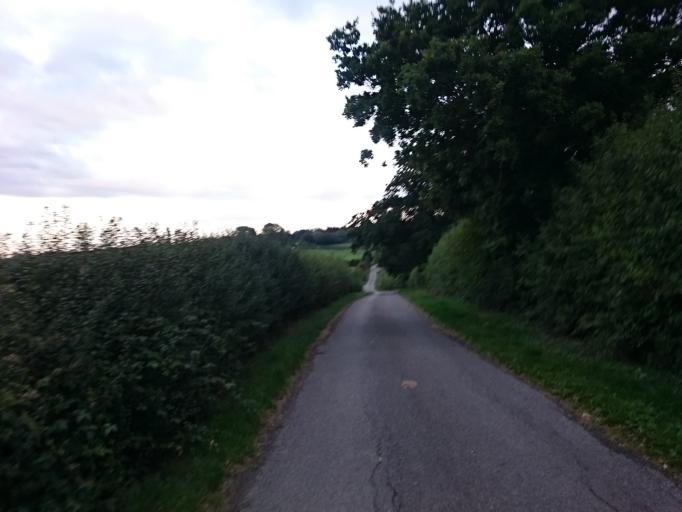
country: GB
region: England
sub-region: Oxfordshire
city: Boars Hill
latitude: 51.7249
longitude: -1.2828
